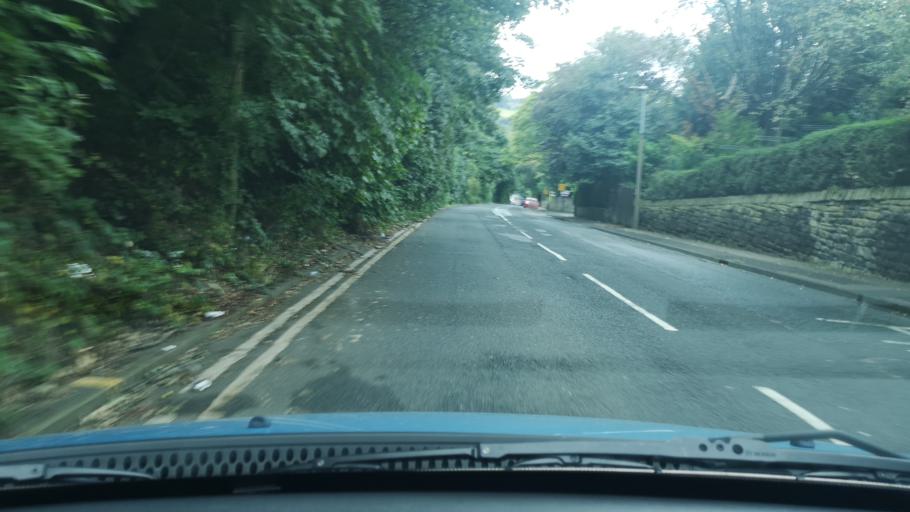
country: GB
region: England
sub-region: Kirklees
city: Batley
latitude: 53.7223
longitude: -1.6385
